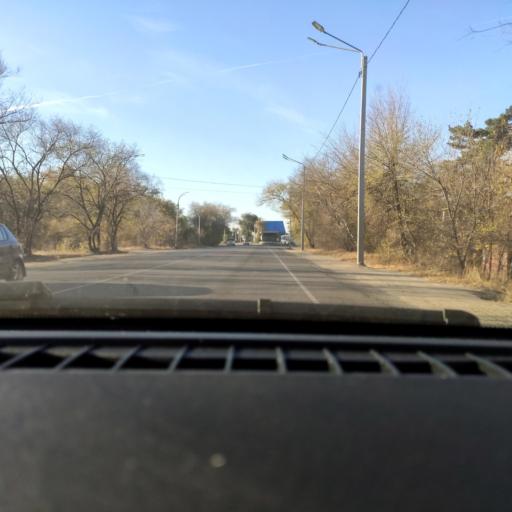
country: RU
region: Voronezj
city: Maslovka
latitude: 51.6328
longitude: 39.2882
